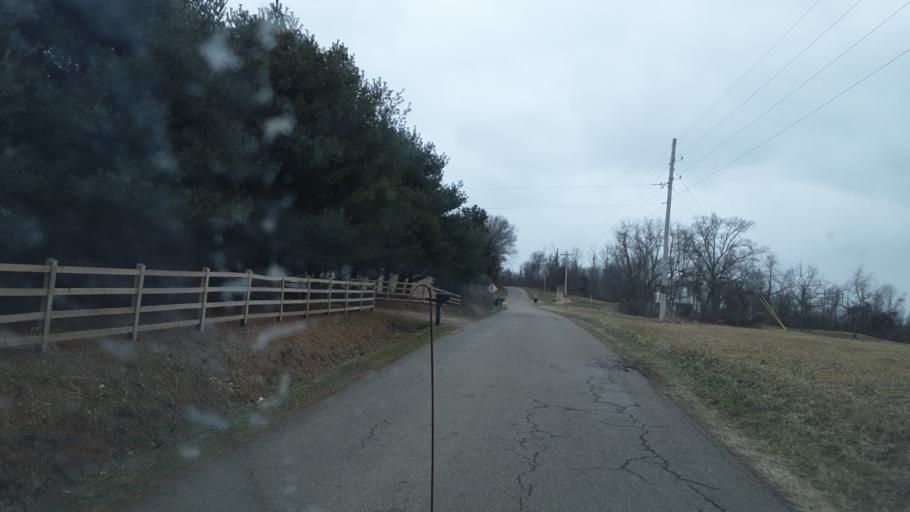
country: US
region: Ohio
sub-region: Perry County
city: Thornport
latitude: 39.9347
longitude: -82.3643
